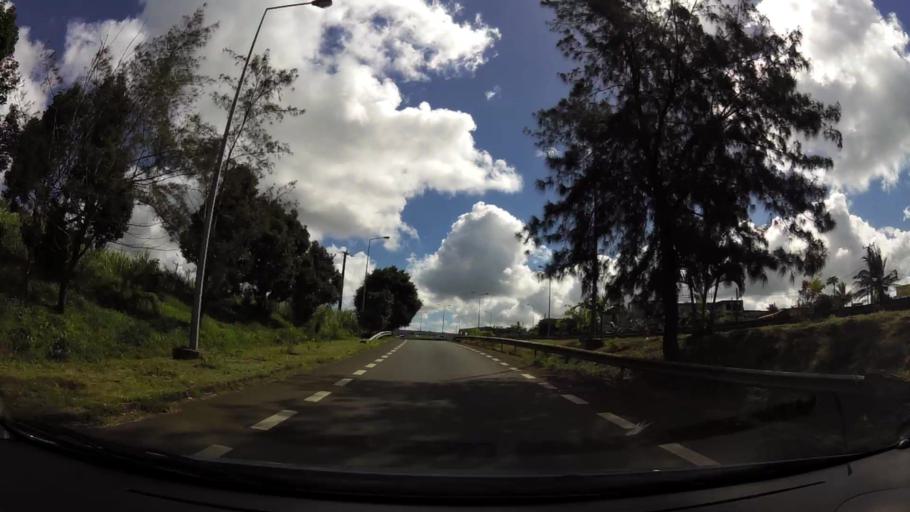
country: MU
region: Grand Port
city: Rose Belle
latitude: -20.4034
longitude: 57.5943
